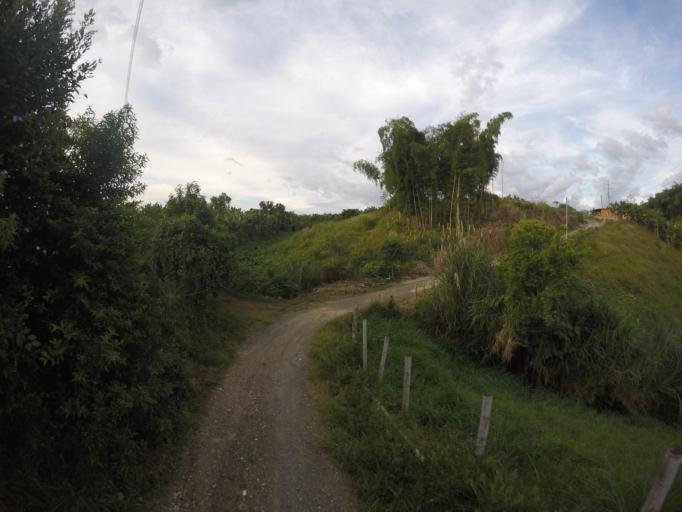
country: CO
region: Valle del Cauca
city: Ulloa
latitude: 4.7136
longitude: -75.7324
